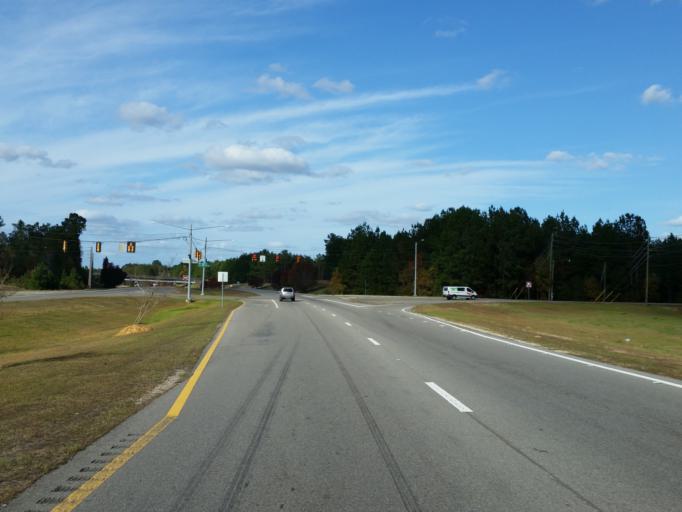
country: US
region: Mississippi
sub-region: Forrest County
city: Hattiesburg
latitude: 31.2881
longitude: -89.3224
